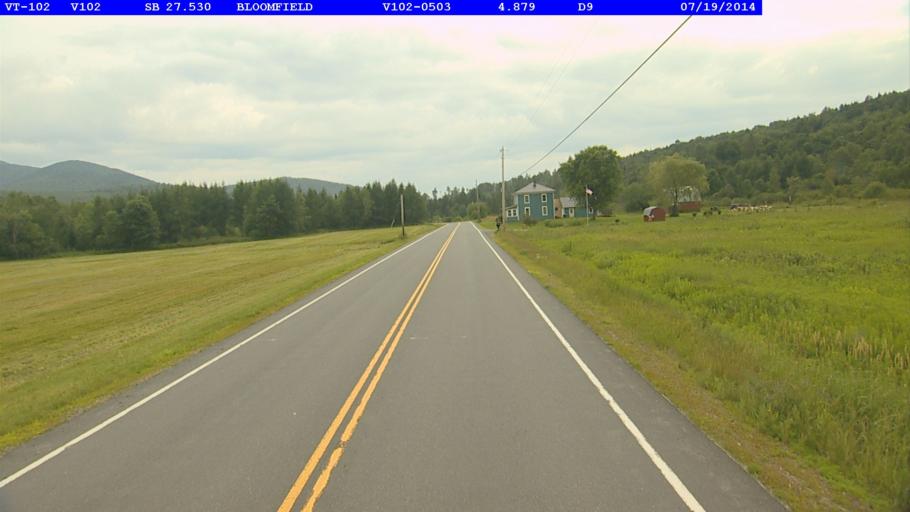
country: US
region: New Hampshire
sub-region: Coos County
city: Colebrook
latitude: 44.8010
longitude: -71.5738
